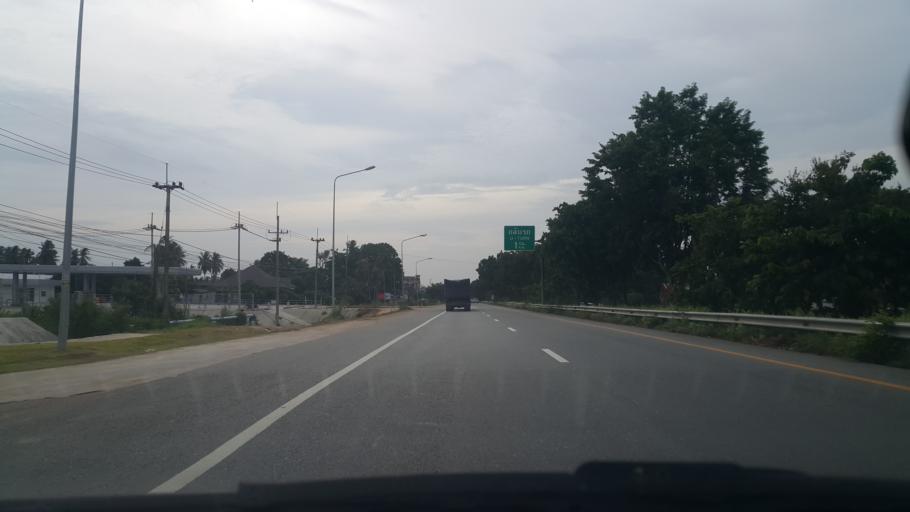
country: TH
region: Chon Buri
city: Bang Lamung
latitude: 12.9737
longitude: 100.9675
